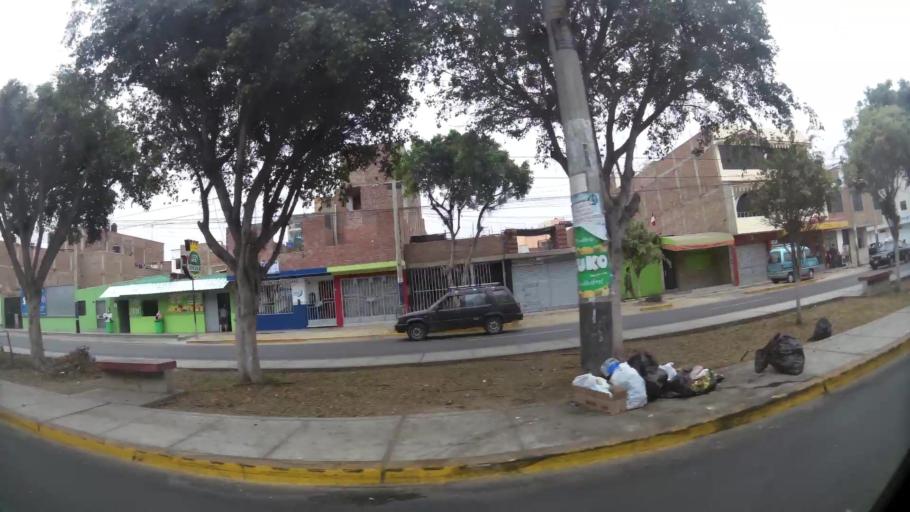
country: PE
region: La Libertad
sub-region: Provincia de Trujillo
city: Trujillo
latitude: -8.1082
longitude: -79.0430
